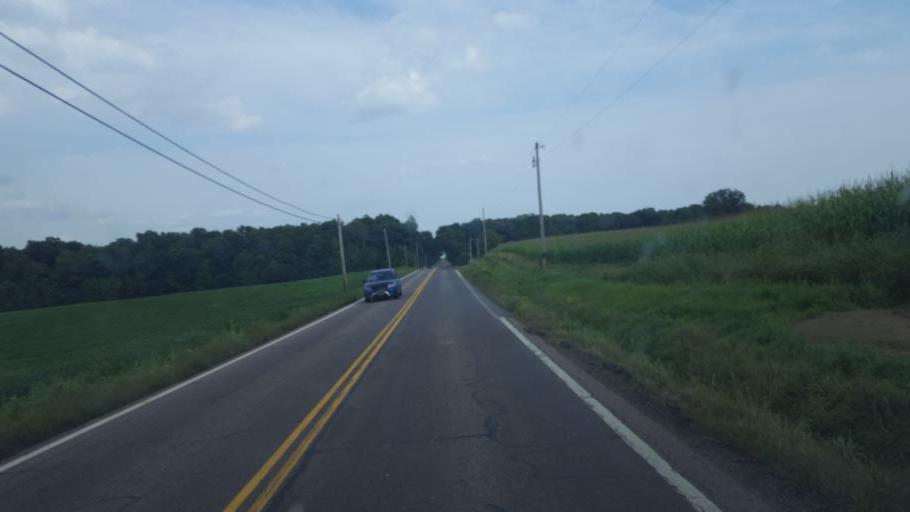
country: US
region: Ohio
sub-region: Knox County
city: Gambier
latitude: 40.3583
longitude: -82.3542
